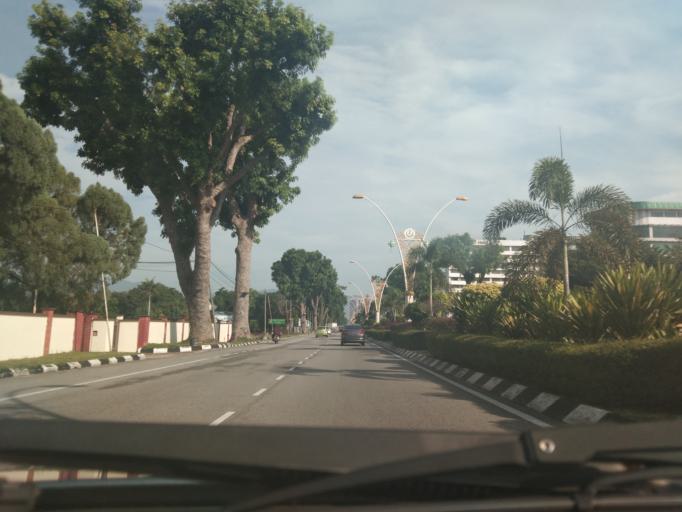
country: MY
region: Perak
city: Ipoh
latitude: 4.5883
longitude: 101.0962
